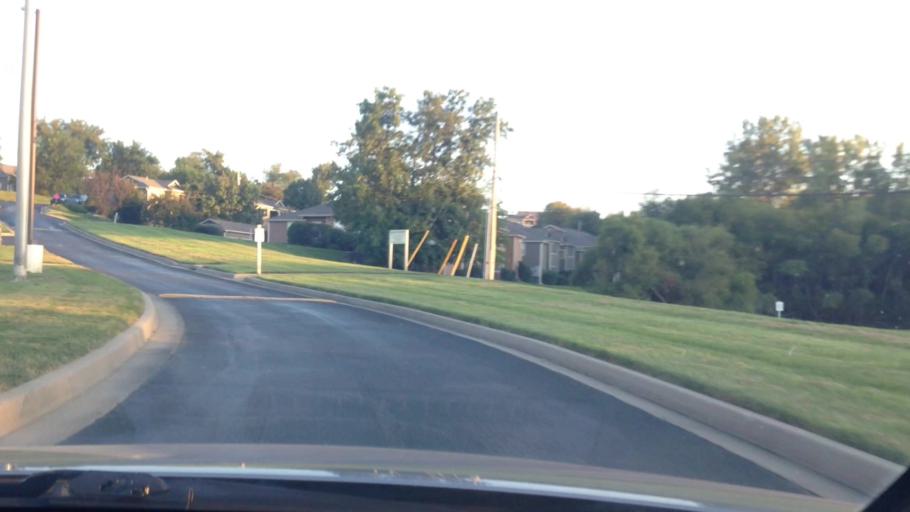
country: US
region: Missouri
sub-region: Jackson County
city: Grandview
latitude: 38.9228
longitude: -94.5593
